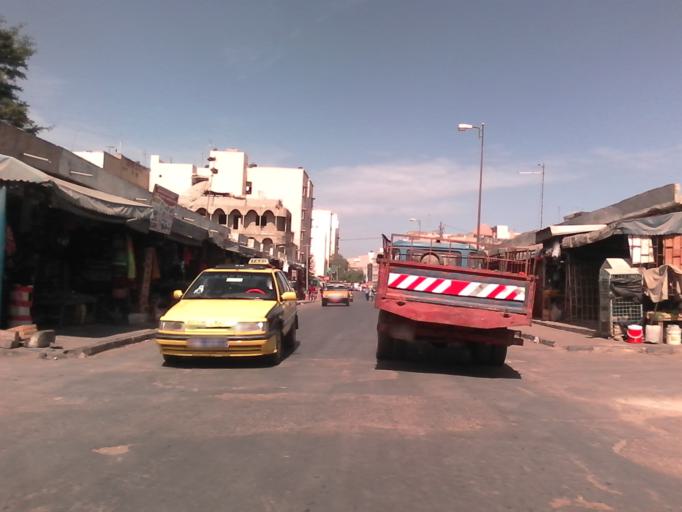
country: SN
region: Dakar
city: Grand Dakar
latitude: 14.7080
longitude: -17.4544
